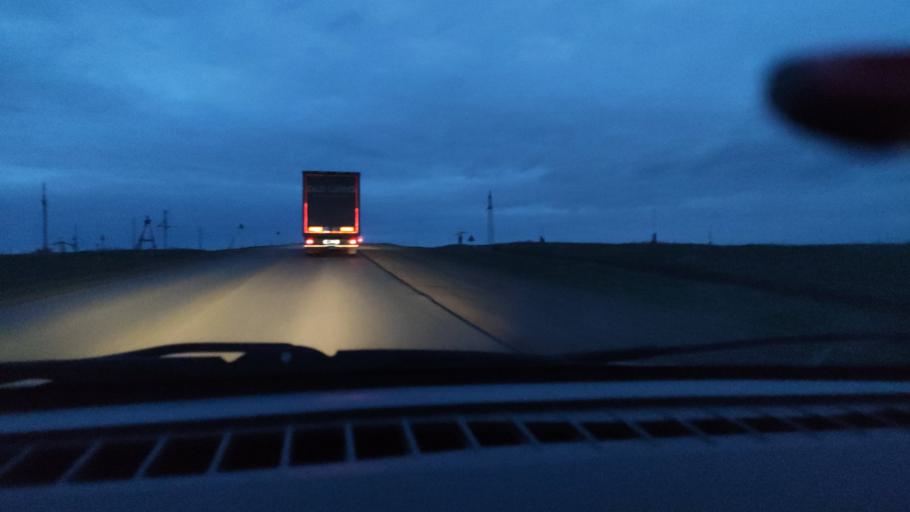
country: RU
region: Orenburg
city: Tatarskaya Kargala
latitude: 51.9551
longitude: 55.1833
